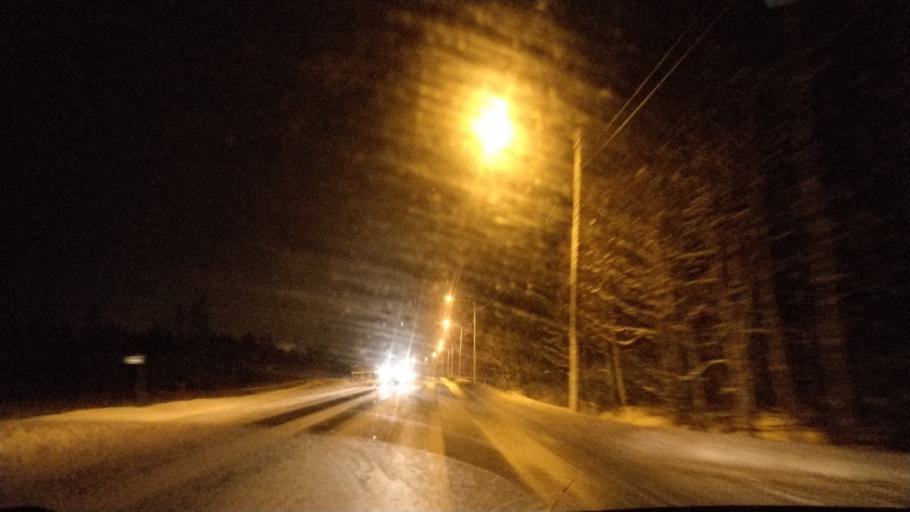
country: FI
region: Lapland
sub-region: Rovaniemi
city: Rovaniemi
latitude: 66.3901
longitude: 25.3785
